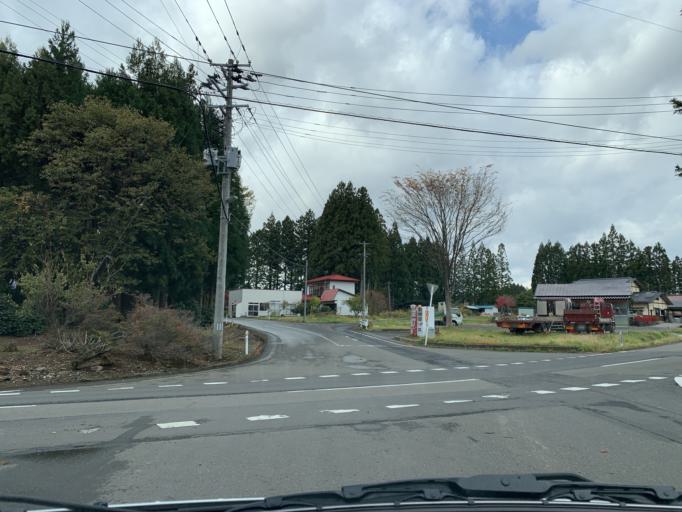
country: JP
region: Iwate
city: Mizusawa
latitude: 39.0729
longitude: 141.0637
